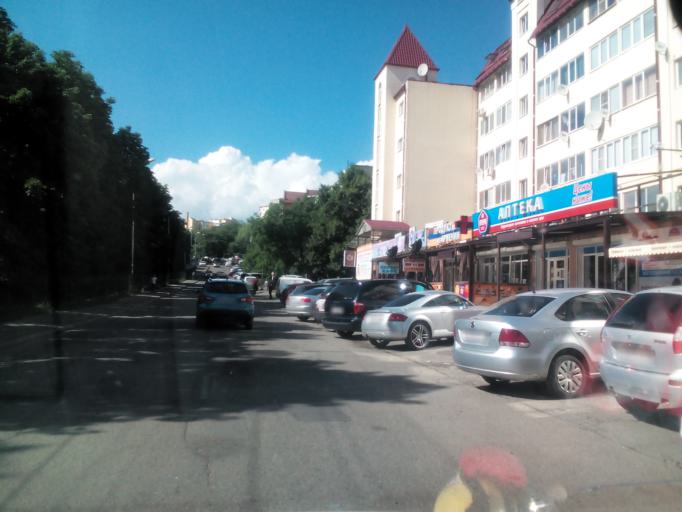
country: RU
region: Stavropol'skiy
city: Pyatigorsk
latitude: 44.0460
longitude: 43.0687
